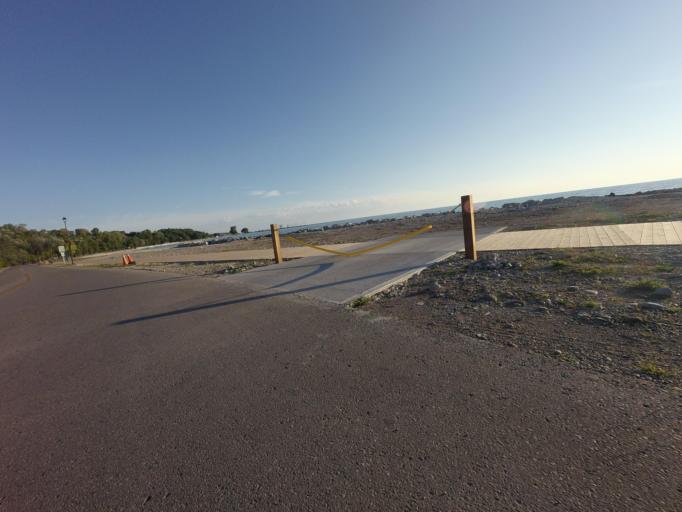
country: CA
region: Ontario
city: Goderich
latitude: 43.7374
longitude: -81.7262
